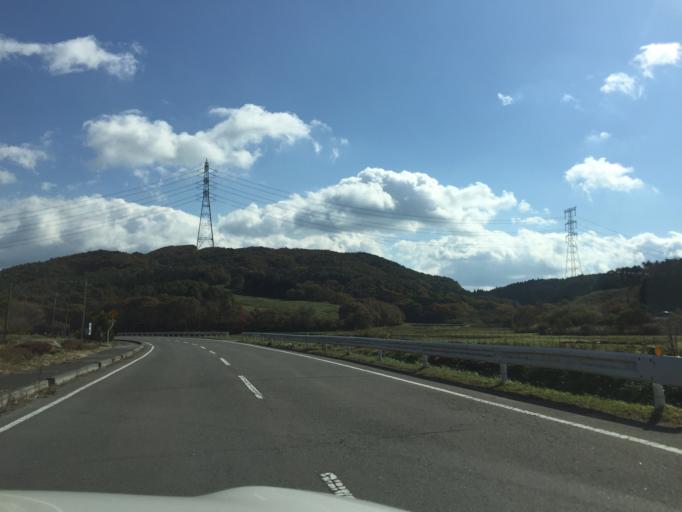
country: JP
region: Fukushima
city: Funehikimachi-funehiki
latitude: 37.2931
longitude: 140.7161
